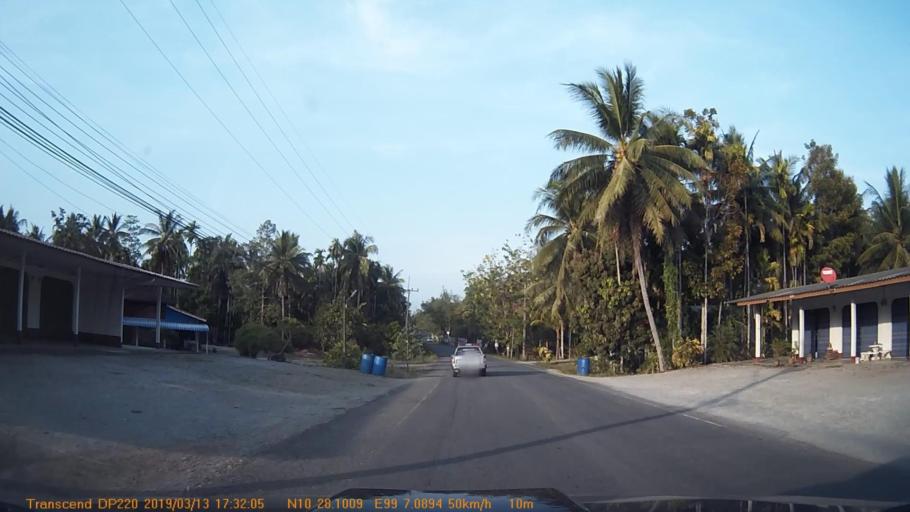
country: TH
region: Chumphon
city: Chumphon
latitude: 10.4686
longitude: 99.1184
